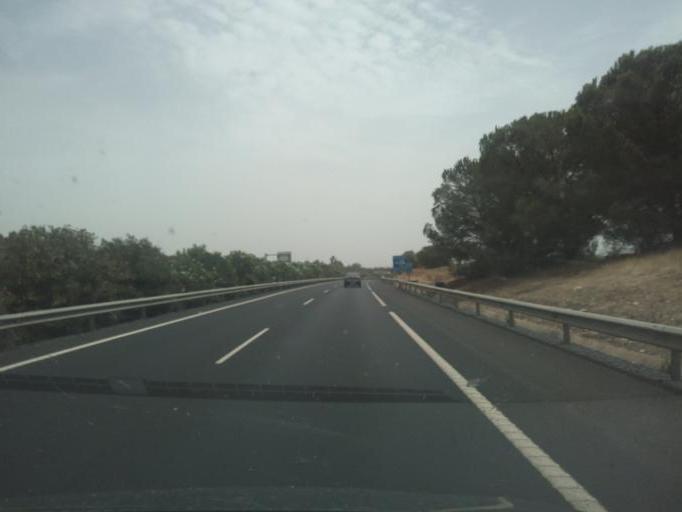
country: ES
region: Andalusia
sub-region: Provincia de Huelva
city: Villarrasa
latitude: 37.3536
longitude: -6.5888
